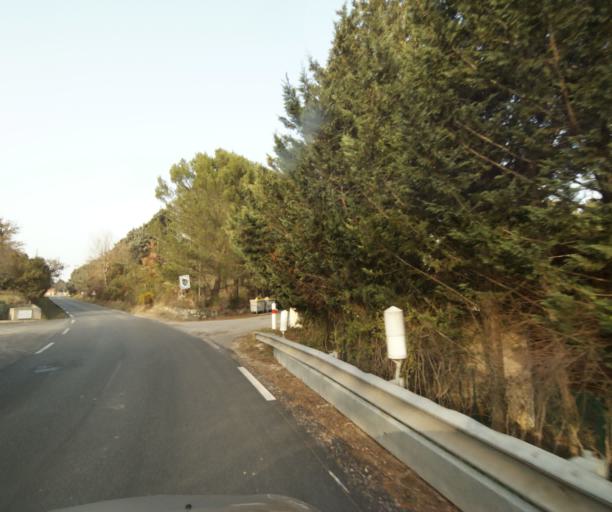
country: FR
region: Provence-Alpes-Cote d'Azur
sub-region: Departement des Bouches-du-Rhone
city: Eguilles
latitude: 43.5836
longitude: 5.3696
